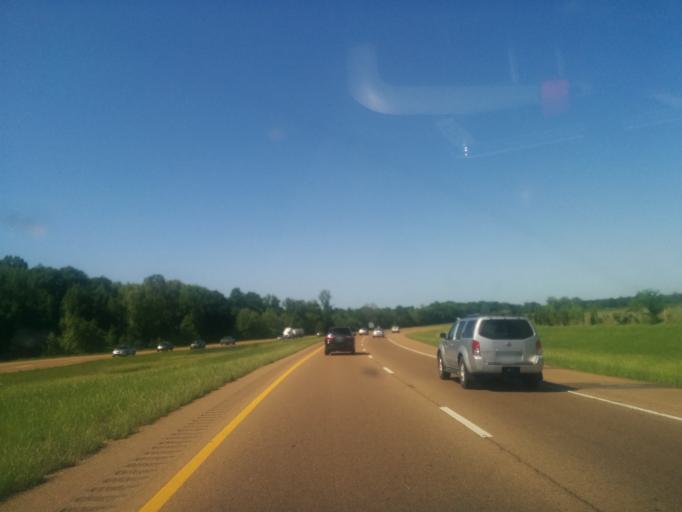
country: US
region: Mississippi
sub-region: Madison County
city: Madison
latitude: 32.4840
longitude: -90.1305
